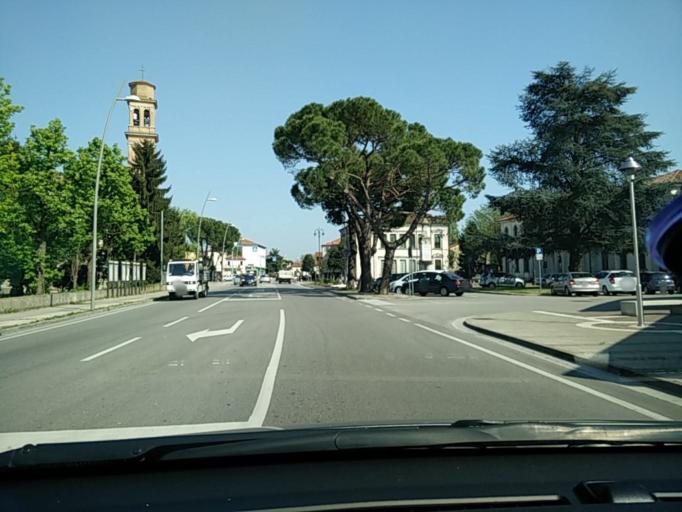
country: IT
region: Veneto
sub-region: Provincia di Venezia
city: Fiesso d'Artico
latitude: 45.4170
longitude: 12.0296
